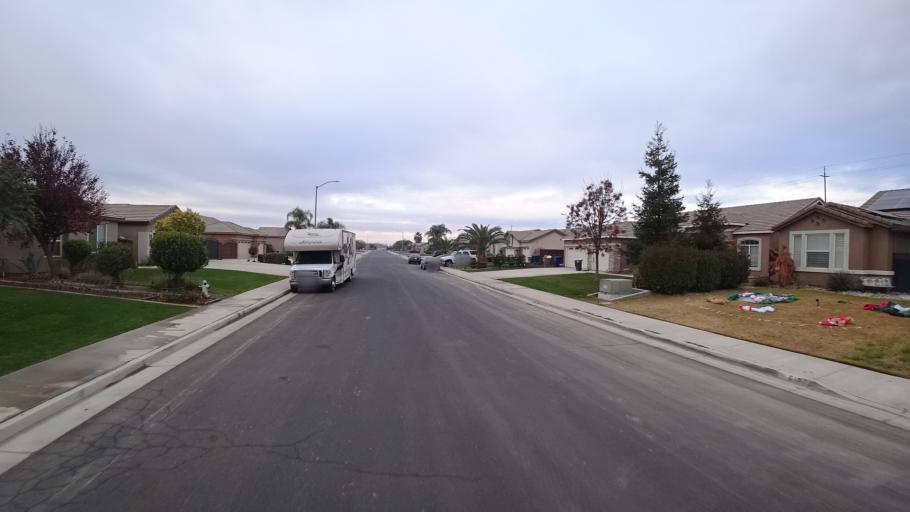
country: US
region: California
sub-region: Kern County
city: Greenfield
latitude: 35.2953
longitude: -119.0704
